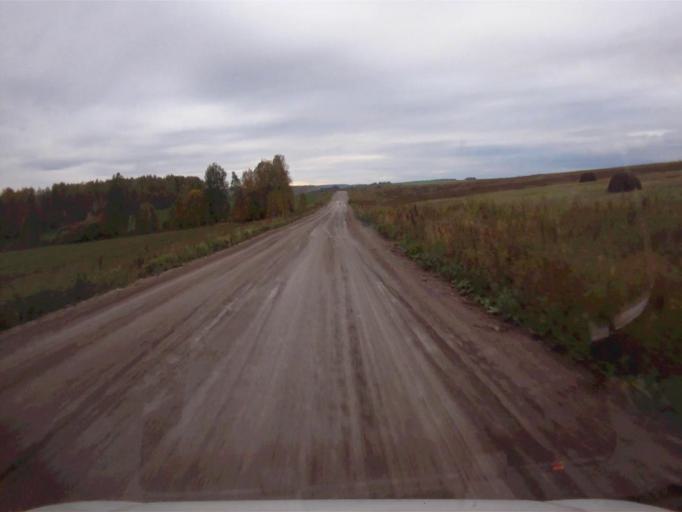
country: RU
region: Sverdlovsk
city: Mikhaylovsk
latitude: 56.1780
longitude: 59.2039
